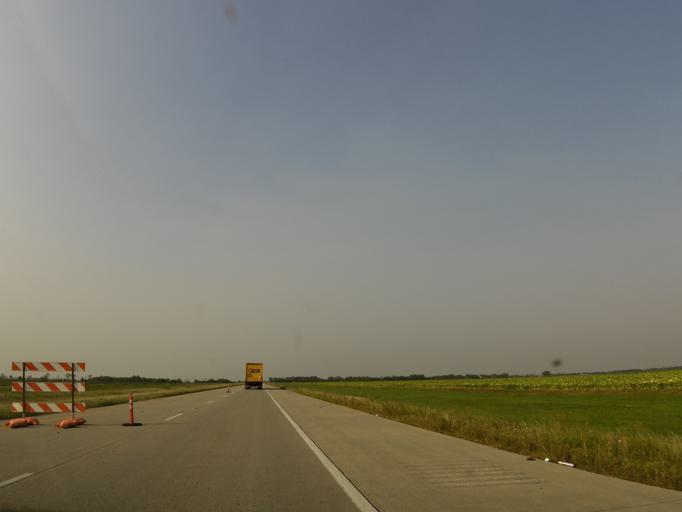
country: US
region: North Dakota
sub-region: Cass County
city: Horace
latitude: 46.6963
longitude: -96.8305
